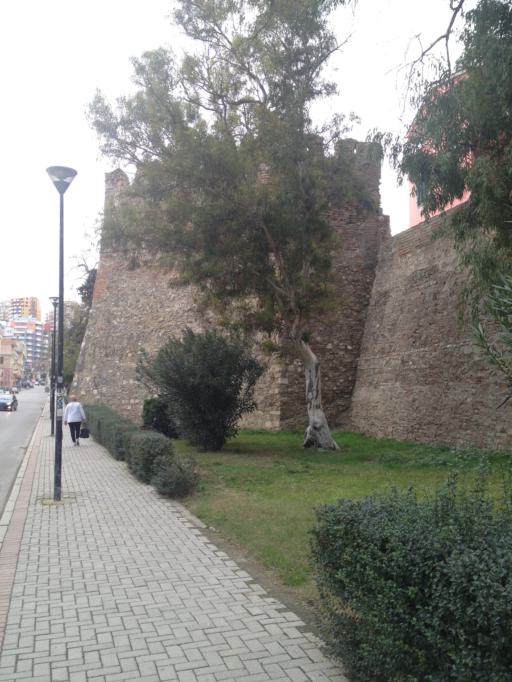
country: AL
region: Durres
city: Durres
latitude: 41.3100
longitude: 19.4465
